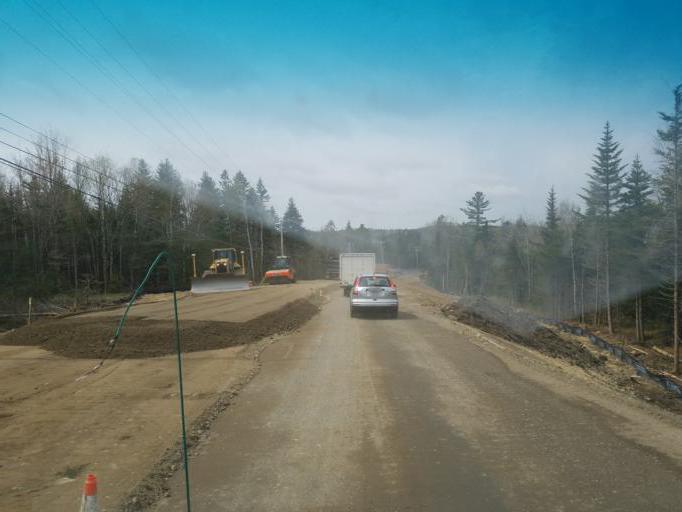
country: US
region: Maine
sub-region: Washington County
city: East Machias
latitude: 44.7675
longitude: -67.1988
